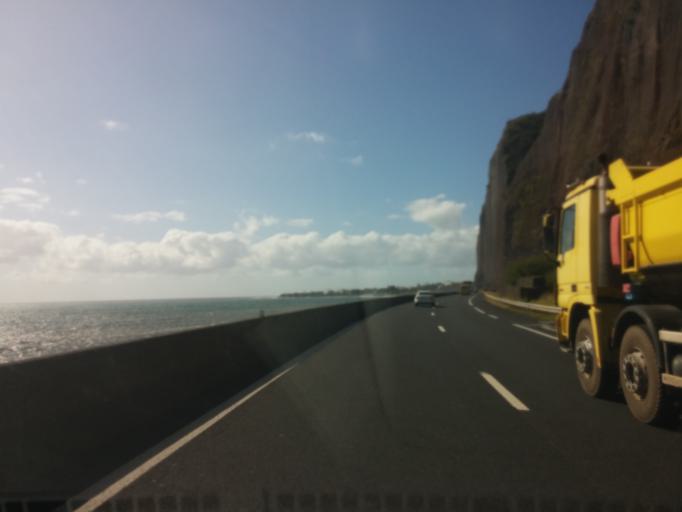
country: RE
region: Reunion
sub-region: Reunion
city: Saint-Denis
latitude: -20.8747
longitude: 55.4262
